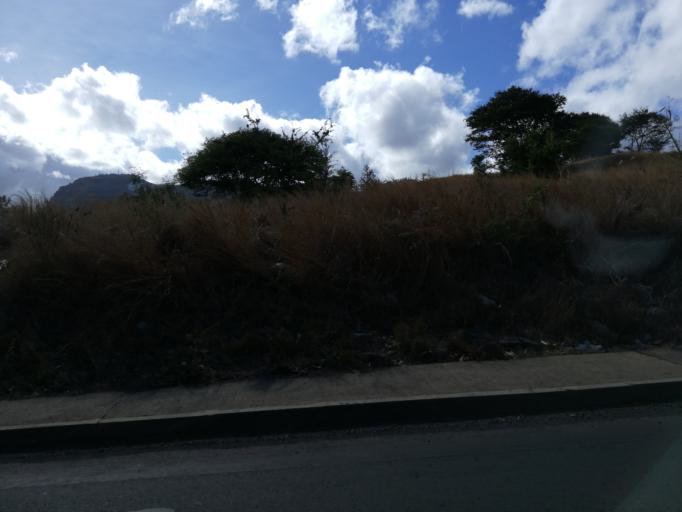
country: MU
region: Moka
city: Pailles
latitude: -20.1788
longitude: 57.4740
